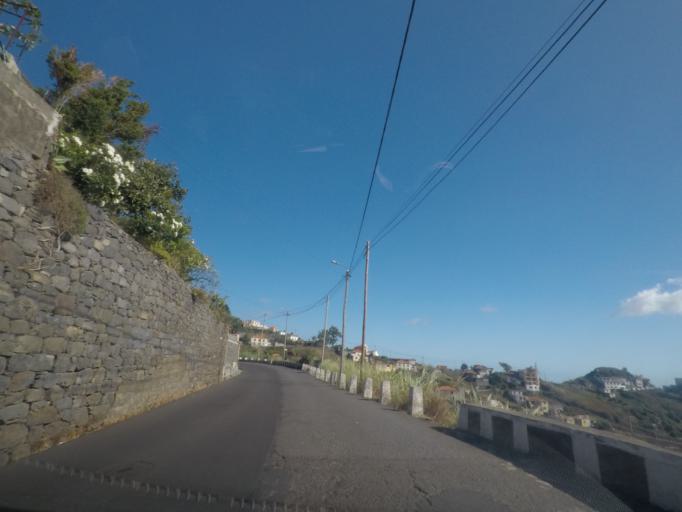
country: PT
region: Madeira
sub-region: Ribeira Brava
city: Campanario
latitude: 32.6637
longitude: -17.0206
